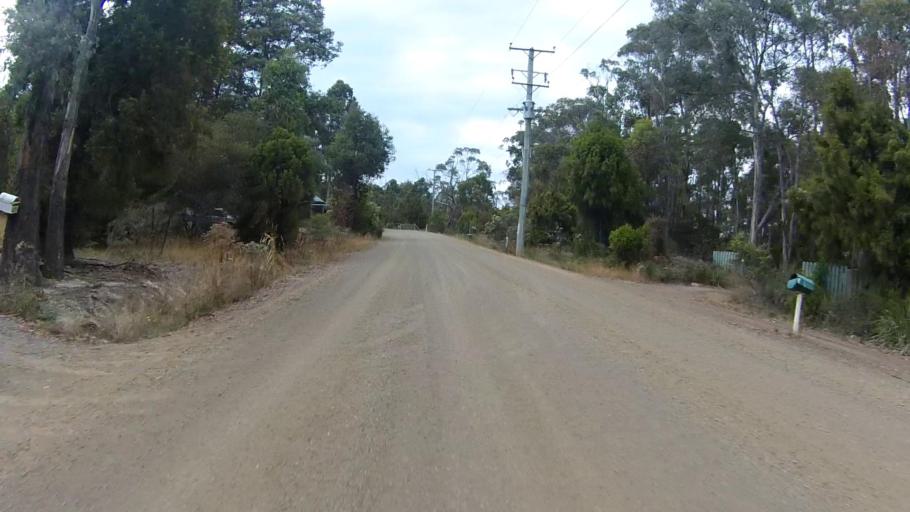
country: AU
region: Tasmania
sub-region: Huon Valley
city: Cygnet
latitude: -43.2298
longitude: 147.0971
